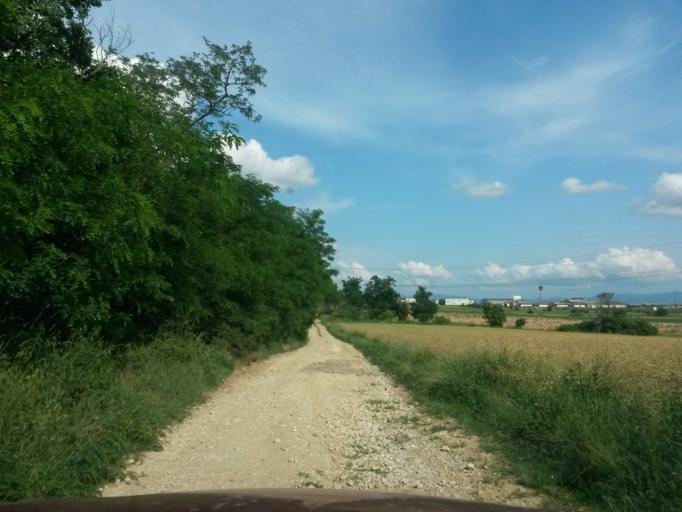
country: SK
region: Kosicky
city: Moldava nad Bodvou
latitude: 48.6093
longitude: 21.1030
